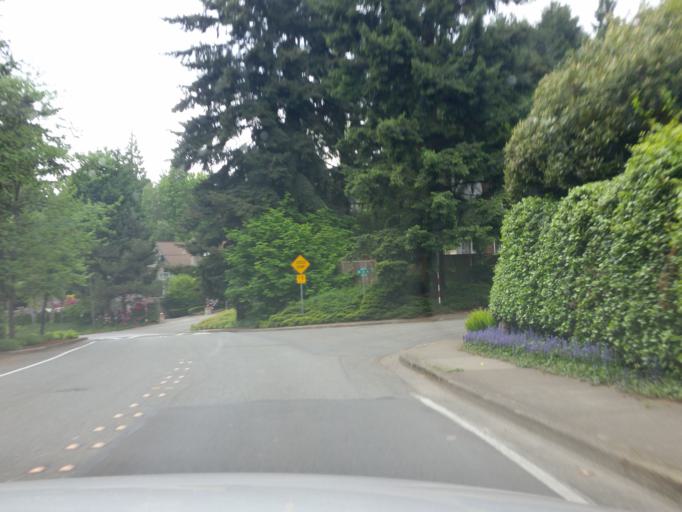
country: US
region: Washington
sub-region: King County
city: Yarrow Point
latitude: 47.6450
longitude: -122.1921
